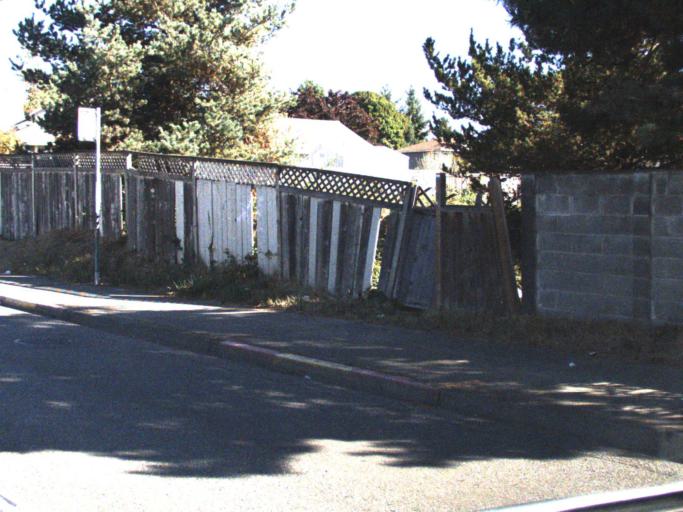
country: US
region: Washington
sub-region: King County
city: East Hill-Meridian
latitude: 47.4052
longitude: -122.1971
